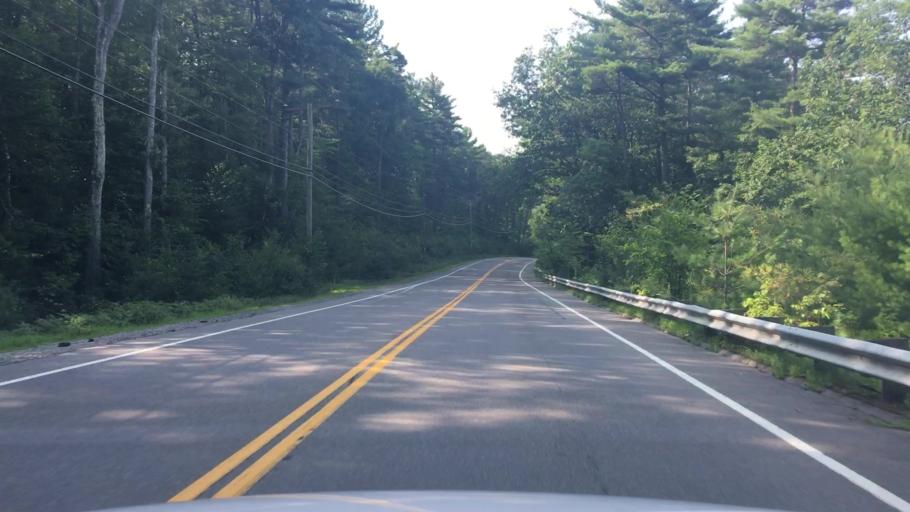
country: US
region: New Hampshire
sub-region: Rockingham County
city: Auburn
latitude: 42.9898
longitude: -71.3775
